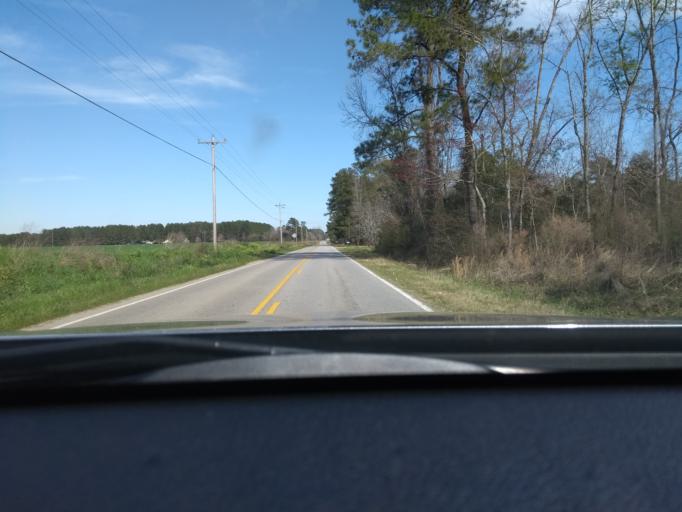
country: US
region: Georgia
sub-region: Bulloch County
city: Brooklet
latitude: 32.4186
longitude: -81.7106
